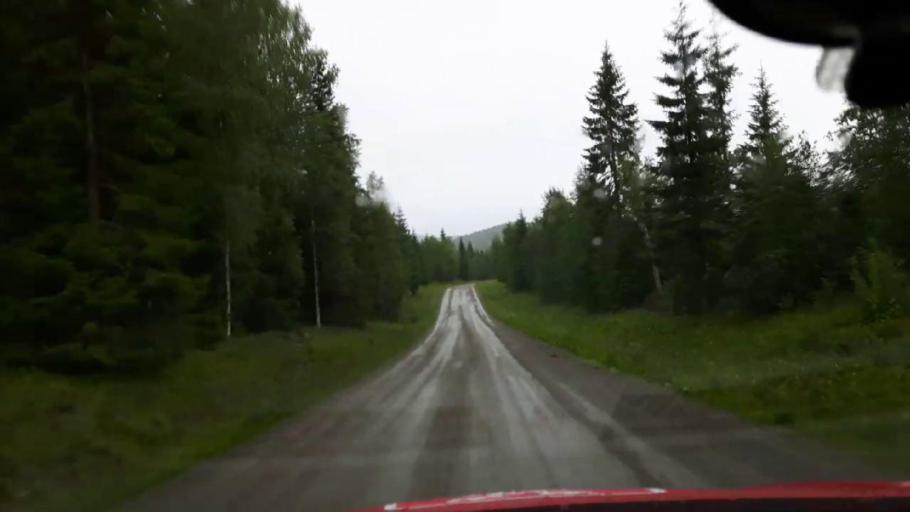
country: SE
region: Jaemtland
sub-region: OEstersunds Kommun
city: Brunflo
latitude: 62.8478
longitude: 14.9735
